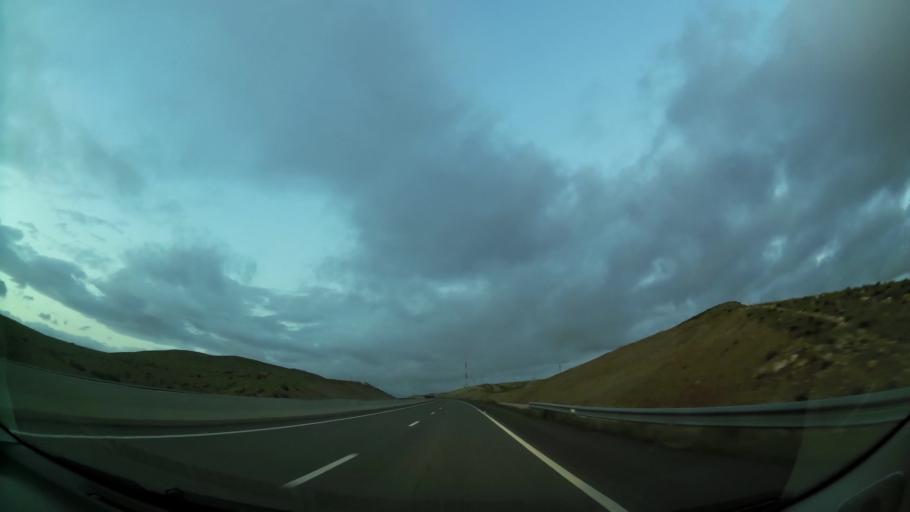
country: MA
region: Oriental
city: El Aioun
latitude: 34.6156
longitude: -2.4137
